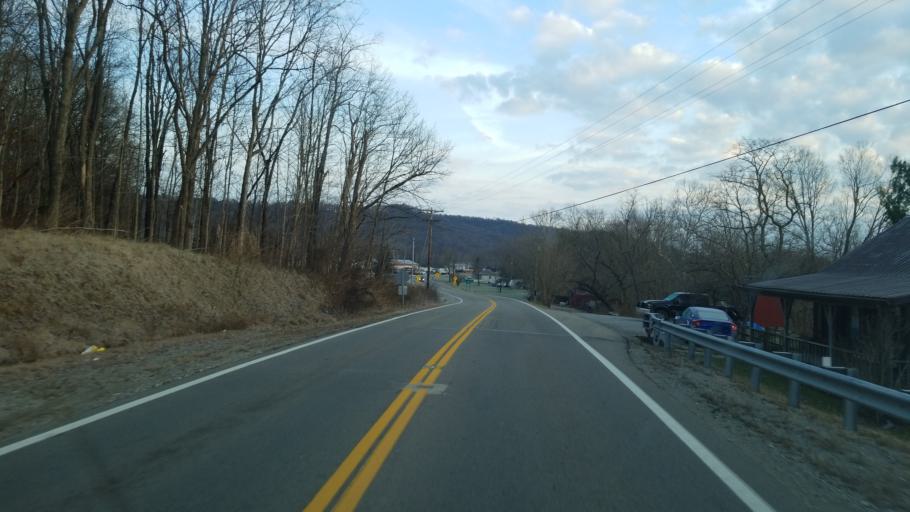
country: US
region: Ohio
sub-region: Ross County
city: Frankfort
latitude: 39.2498
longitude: -83.2044
